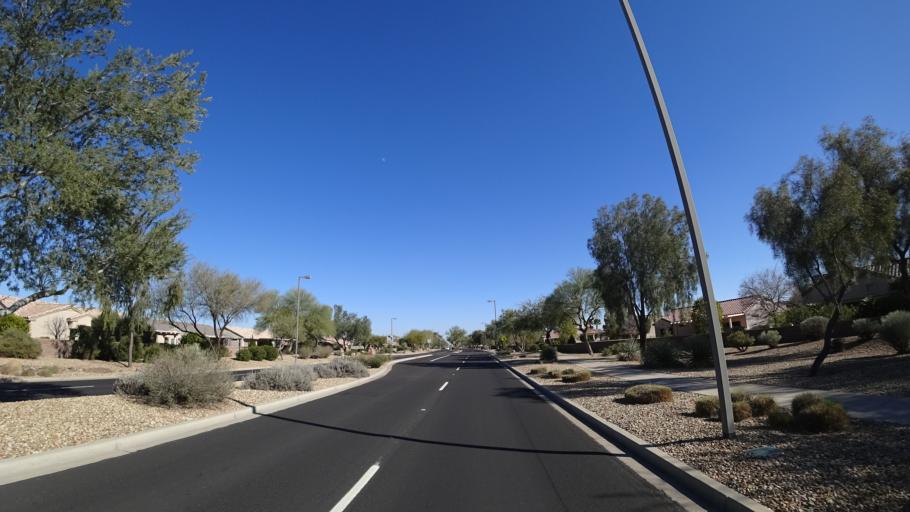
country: US
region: Arizona
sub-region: Maricopa County
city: Sun City West
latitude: 33.6553
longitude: -112.4078
